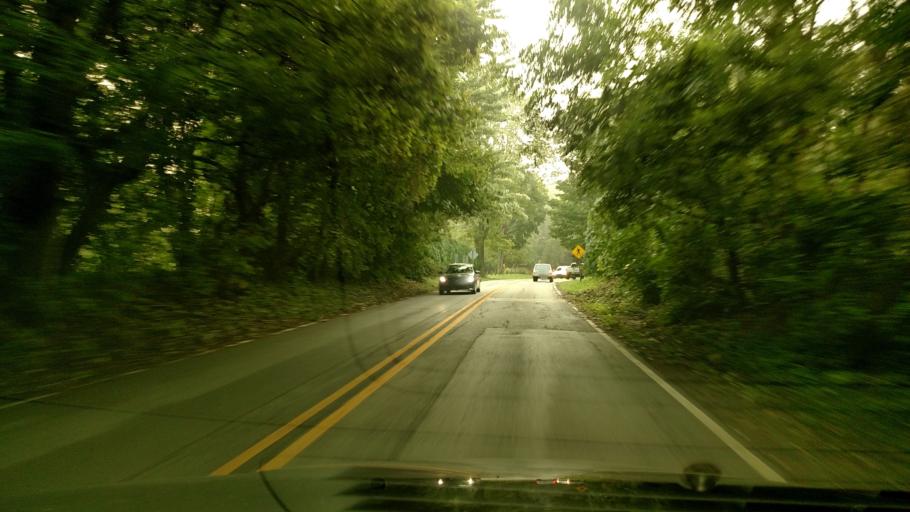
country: US
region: Indiana
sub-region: Howard County
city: Kokomo
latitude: 40.4620
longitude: -86.1423
